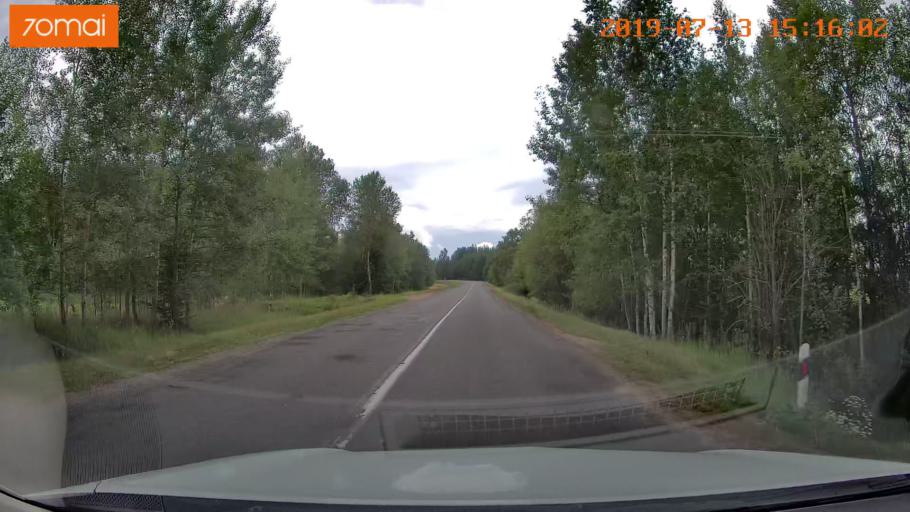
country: BY
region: Mogilev
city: Hlusha
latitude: 53.1118
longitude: 28.8289
